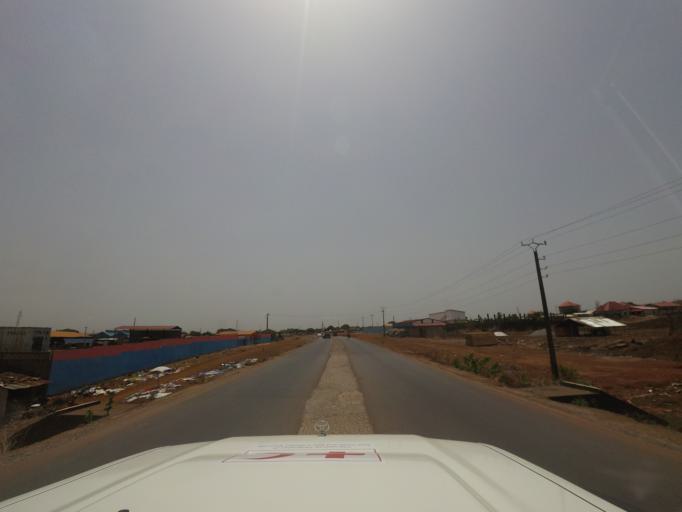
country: GN
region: Kindia
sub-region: Coyah
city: Coyah
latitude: 9.7255
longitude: -13.4495
